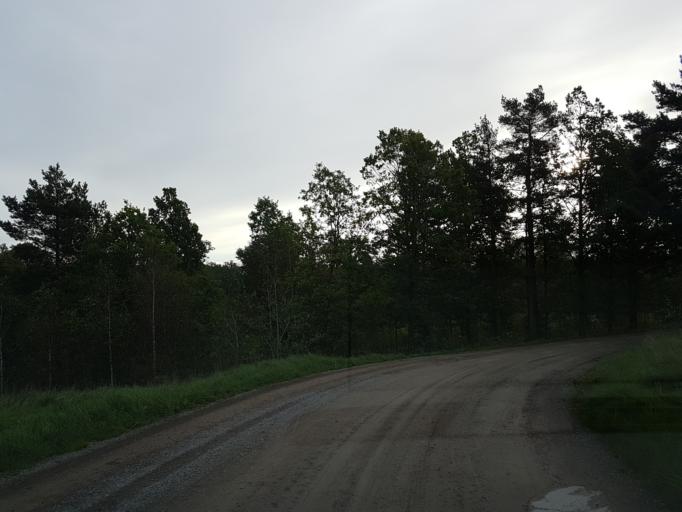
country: SE
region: OEstergoetland
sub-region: Atvidabergs Kommun
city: Atvidaberg
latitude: 58.2130
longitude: 16.0132
